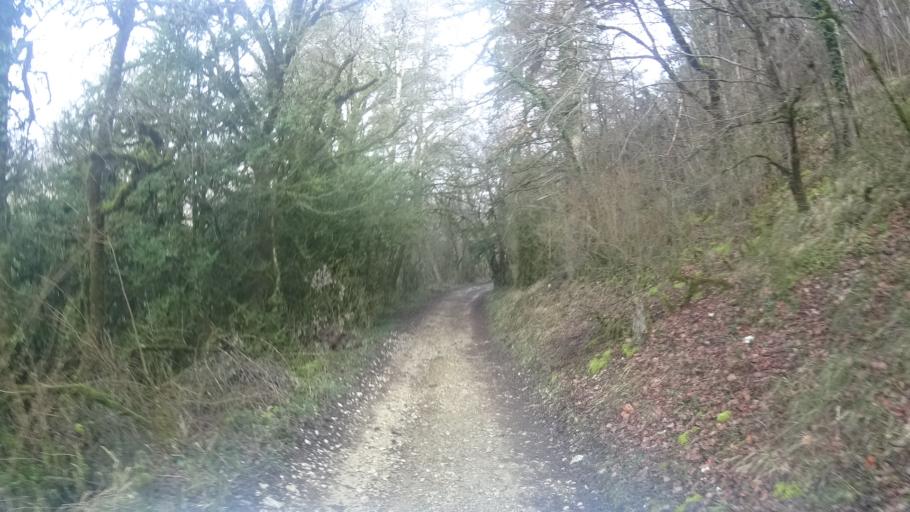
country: FR
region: Aquitaine
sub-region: Departement de la Dordogne
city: Terrasson-Lavilledieu
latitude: 45.0918
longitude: 1.2646
